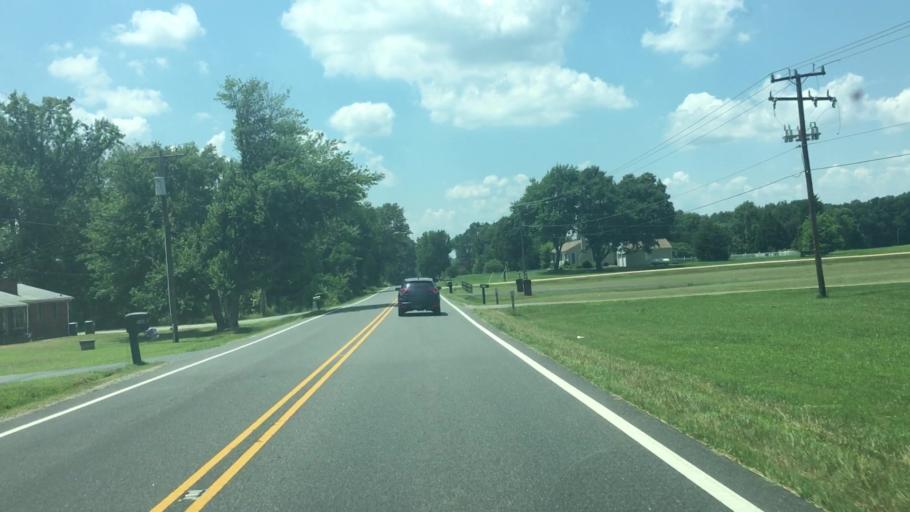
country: US
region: Virginia
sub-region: King George County
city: Passapatanzy
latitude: 38.3015
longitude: -77.3793
